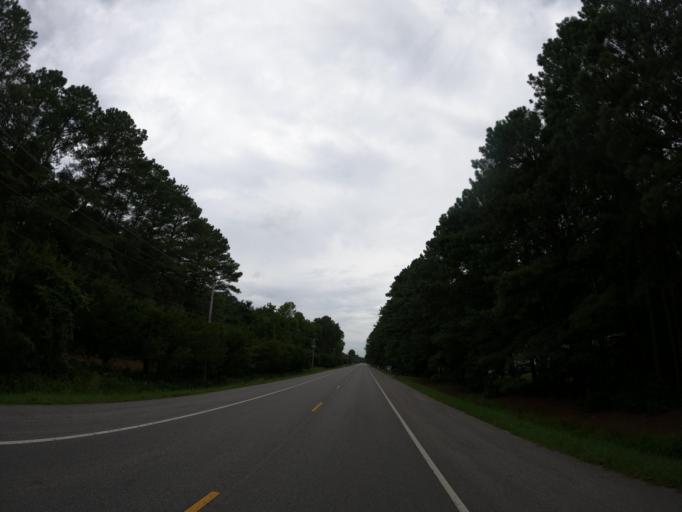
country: US
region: Maryland
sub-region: Saint Mary's County
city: Lexington Park
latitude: 38.1569
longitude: -76.5213
